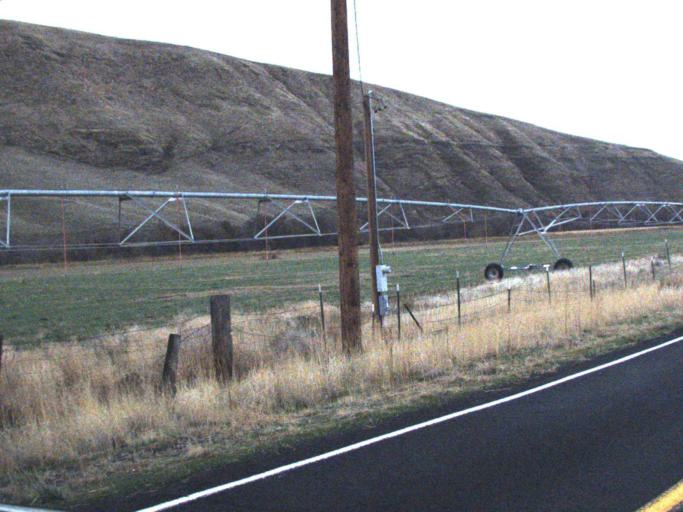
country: US
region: Washington
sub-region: Columbia County
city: Dayton
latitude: 46.5083
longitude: -118.0791
